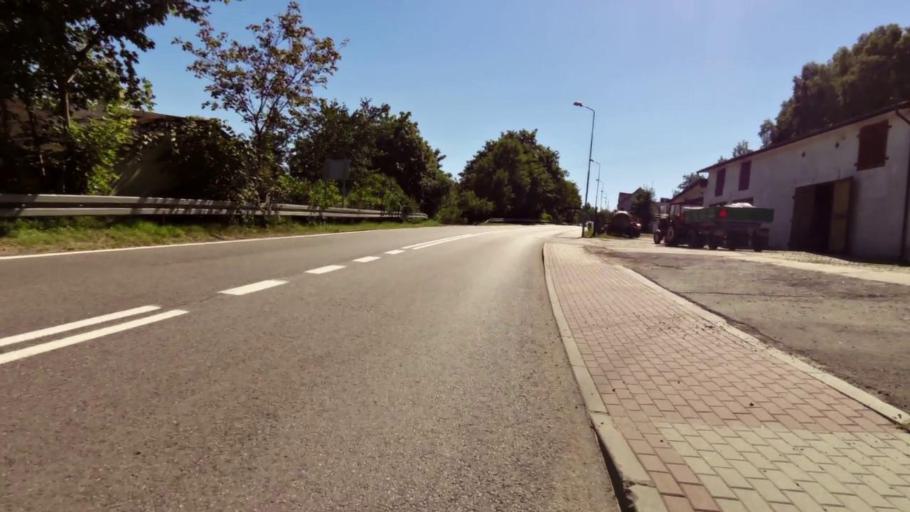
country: PL
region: West Pomeranian Voivodeship
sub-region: Powiat szczecinecki
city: Bialy Bor
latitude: 53.8947
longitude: 16.8316
